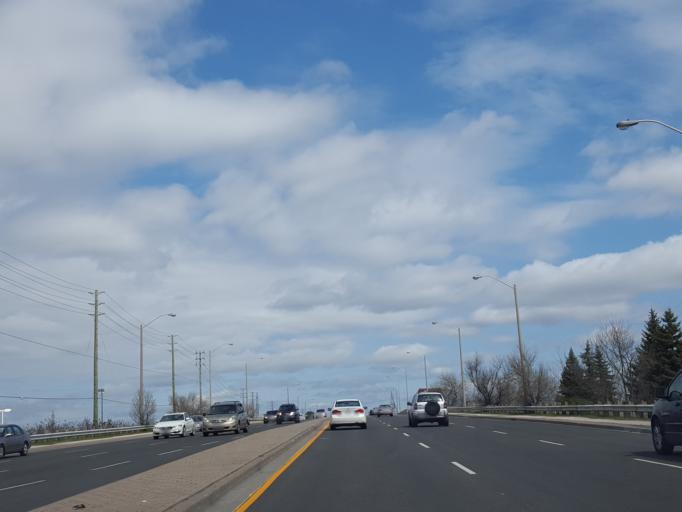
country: CA
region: Ontario
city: Scarborough
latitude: 43.8140
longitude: -79.2433
